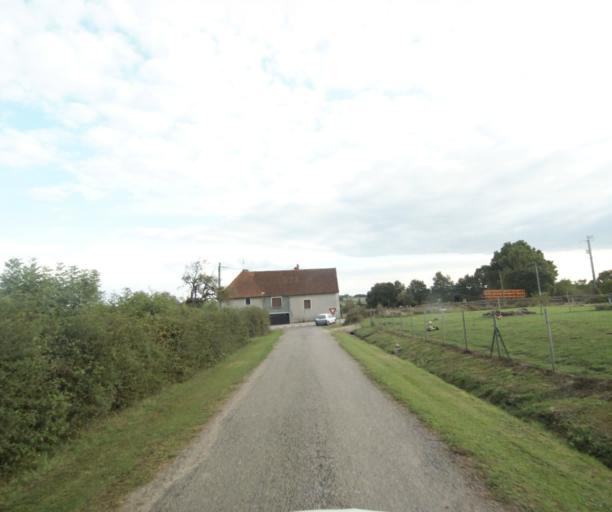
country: FR
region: Bourgogne
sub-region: Departement de Saone-et-Loire
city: Charolles
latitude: 46.4457
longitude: 4.3306
